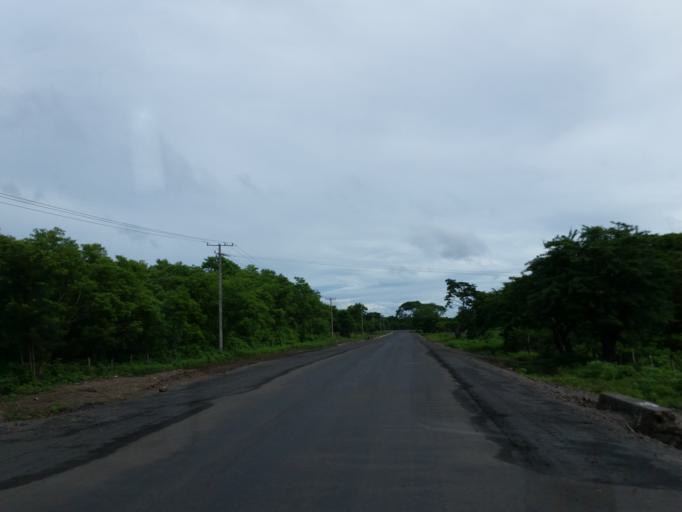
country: NI
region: Leon
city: Larreynaga
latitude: 12.5203
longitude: -86.6019
